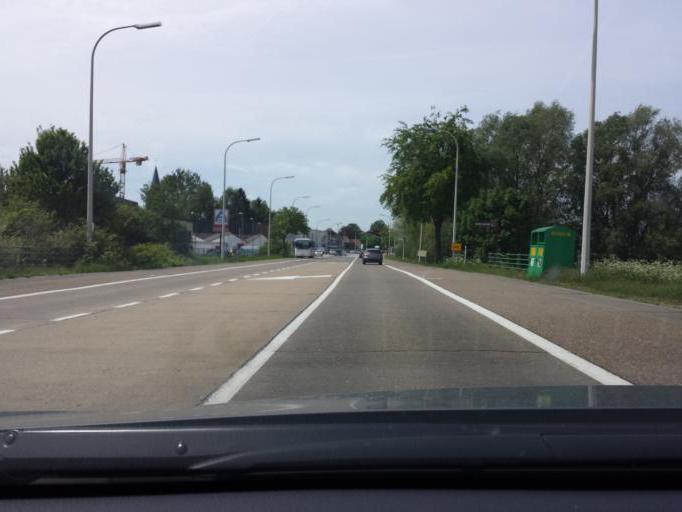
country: BE
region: Flanders
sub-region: Provincie Limburg
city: Halen
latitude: 50.9491
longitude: 5.1197
